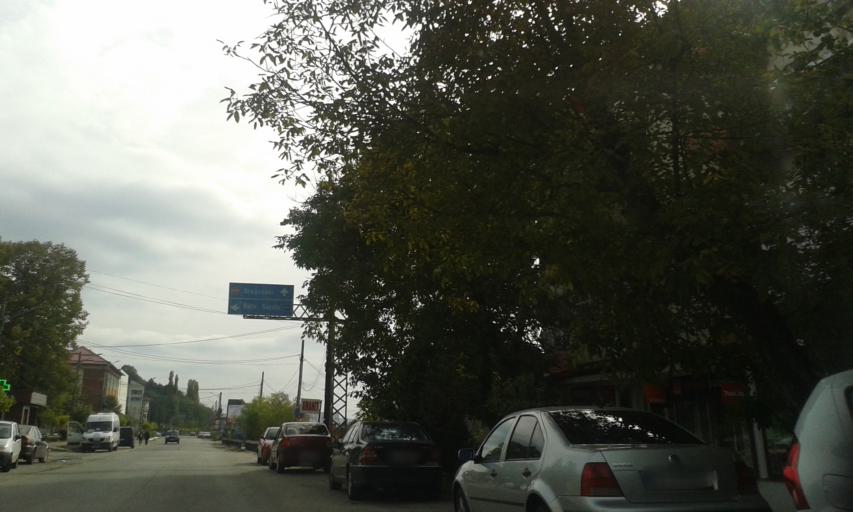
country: RO
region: Gorj
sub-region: Comuna Targu Carbunesti
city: Targu Carbunesti
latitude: 44.9624
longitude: 23.5081
